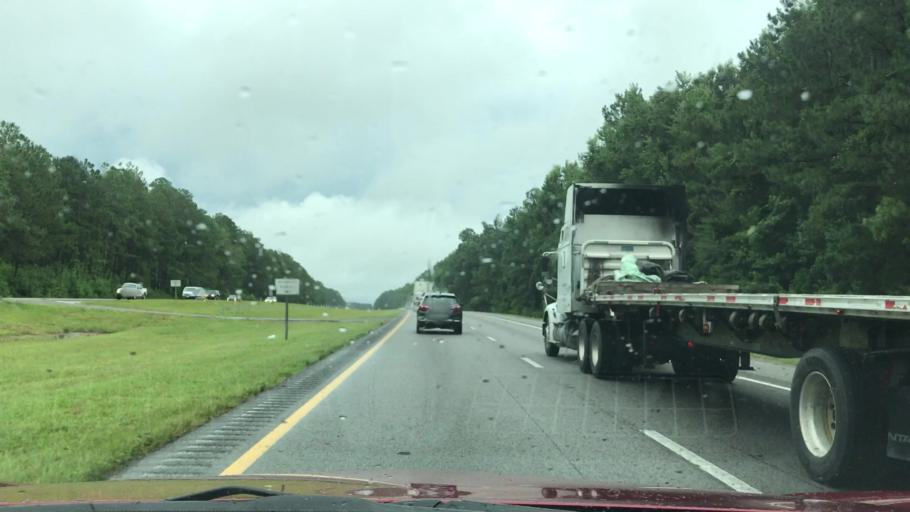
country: US
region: South Carolina
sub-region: Dorchester County
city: Ridgeville
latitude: 33.0938
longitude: -80.2315
